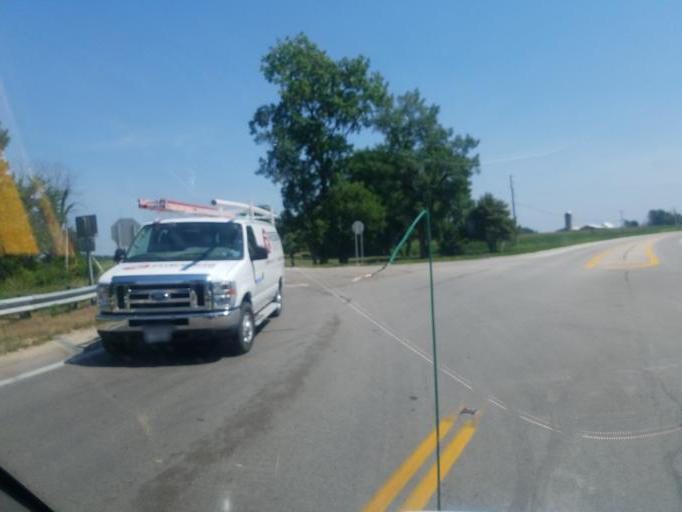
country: US
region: Ohio
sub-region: Mercer County
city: Celina
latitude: 40.4991
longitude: -84.5717
